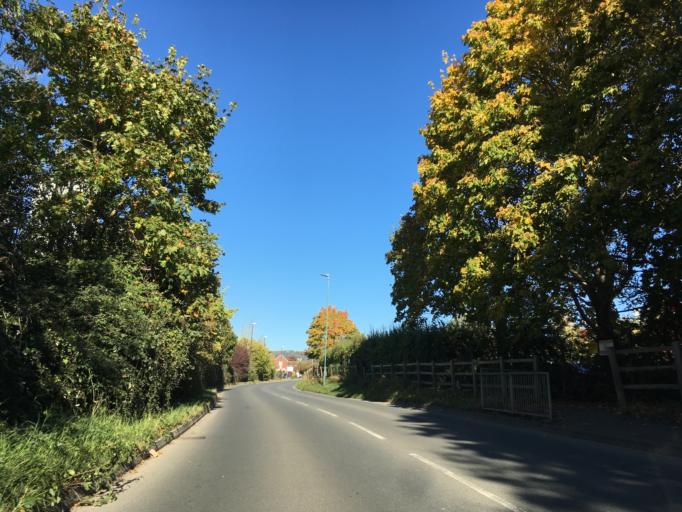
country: GB
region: England
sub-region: Gloucestershire
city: Stonehouse
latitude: 51.7500
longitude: -2.2952
